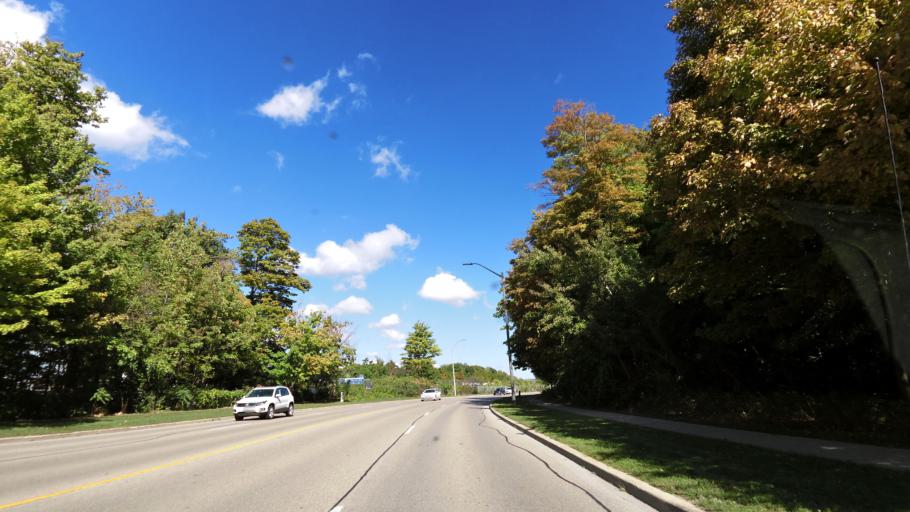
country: CA
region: Ontario
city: Brampton
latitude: 43.6011
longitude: -79.7657
